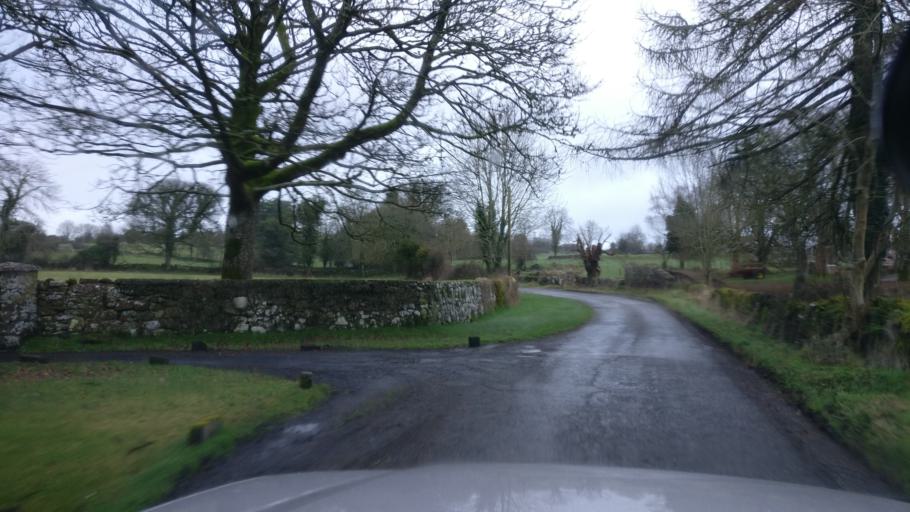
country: IE
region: Connaught
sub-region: County Galway
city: Loughrea
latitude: 53.1800
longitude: -8.6072
